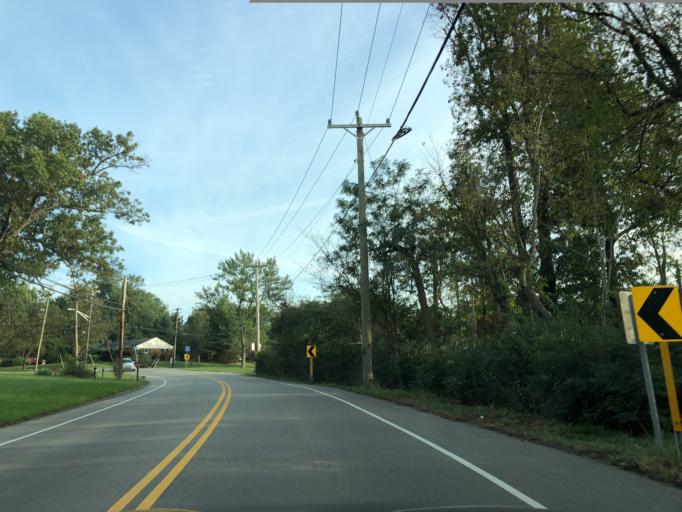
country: US
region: Ohio
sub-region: Warren County
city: Landen
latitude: 39.2827
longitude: -84.2957
